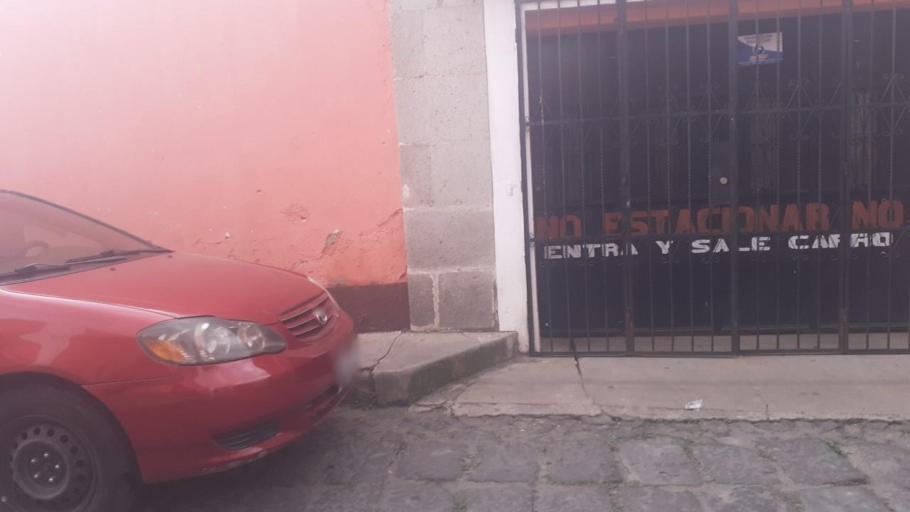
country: GT
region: Quetzaltenango
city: Quetzaltenango
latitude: 14.8375
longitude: -91.5222
